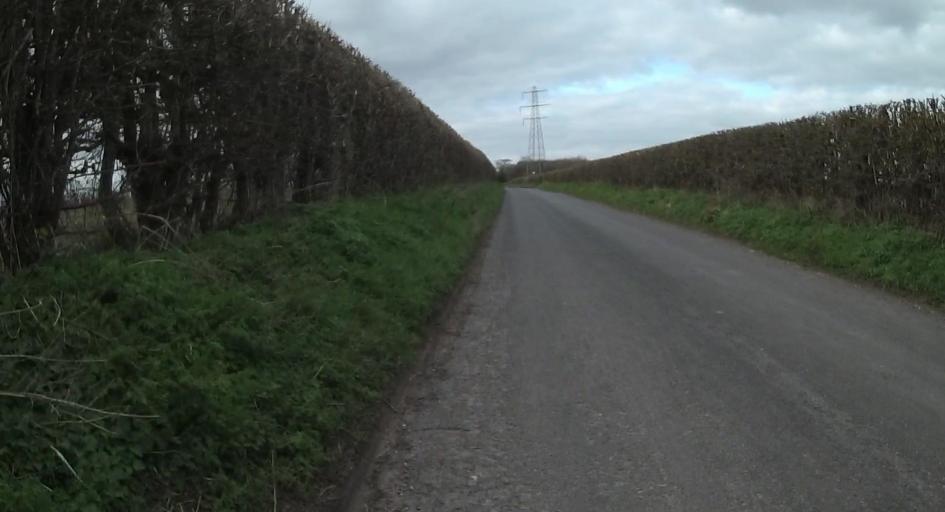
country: GB
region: England
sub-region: Hampshire
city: Abbotts Ann
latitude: 51.1526
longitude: -1.4888
